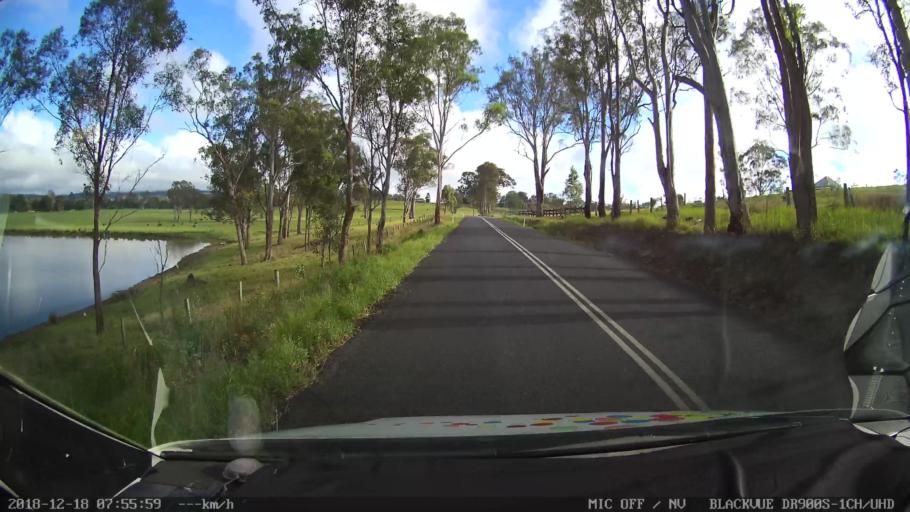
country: AU
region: New South Wales
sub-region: Kyogle
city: Kyogle
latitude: -28.4031
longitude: 152.6035
